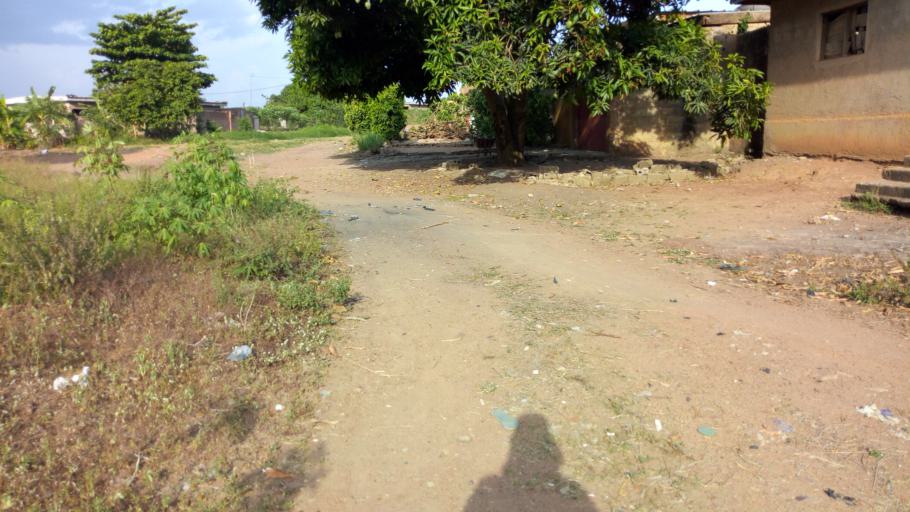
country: CI
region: Vallee du Bandama
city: Bouake
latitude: 7.7091
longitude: -5.0491
